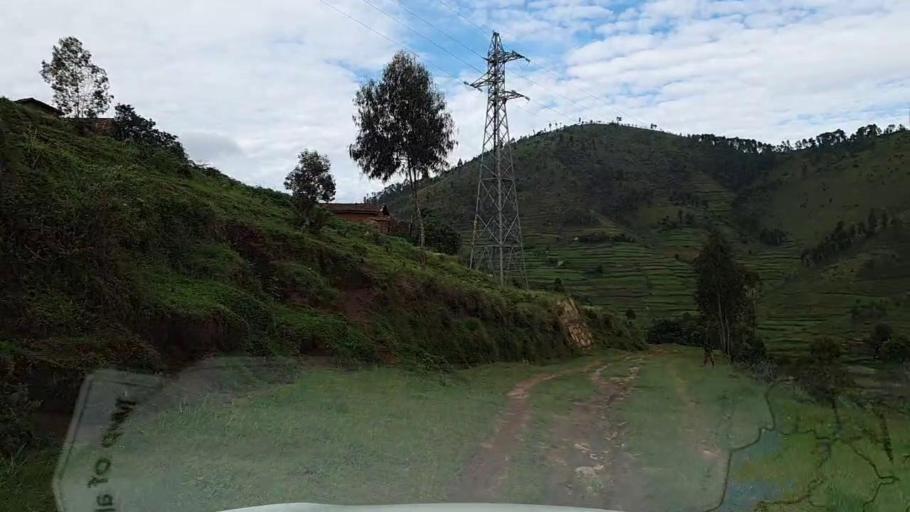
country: RW
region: Southern Province
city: Nzega
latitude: -2.4068
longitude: 29.4965
